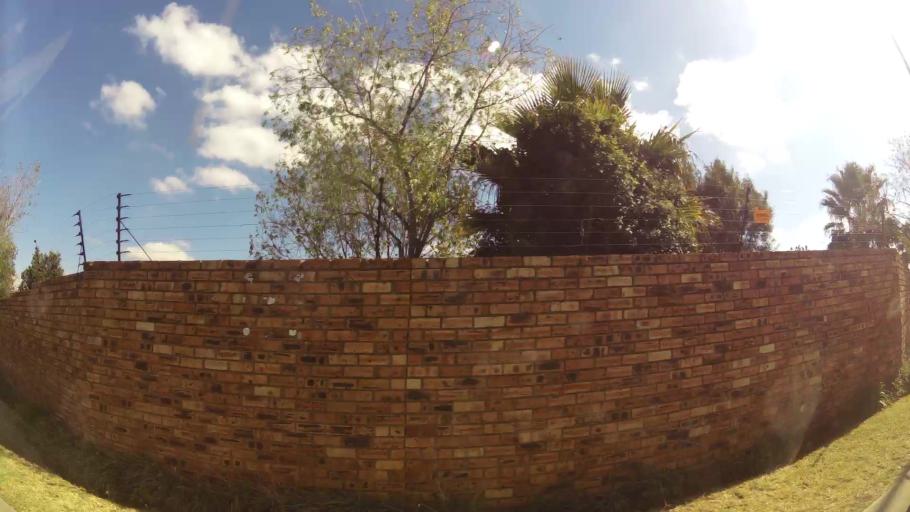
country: ZA
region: Gauteng
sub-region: City of Johannesburg Metropolitan Municipality
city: Midrand
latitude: -25.9942
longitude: 28.1012
